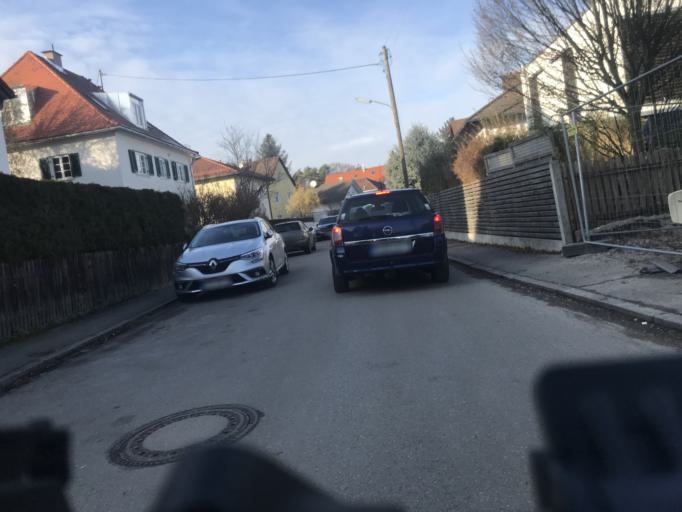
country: DE
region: Bavaria
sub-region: Upper Bavaria
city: Grafelfing
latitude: 48.1362
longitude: 11.4243
